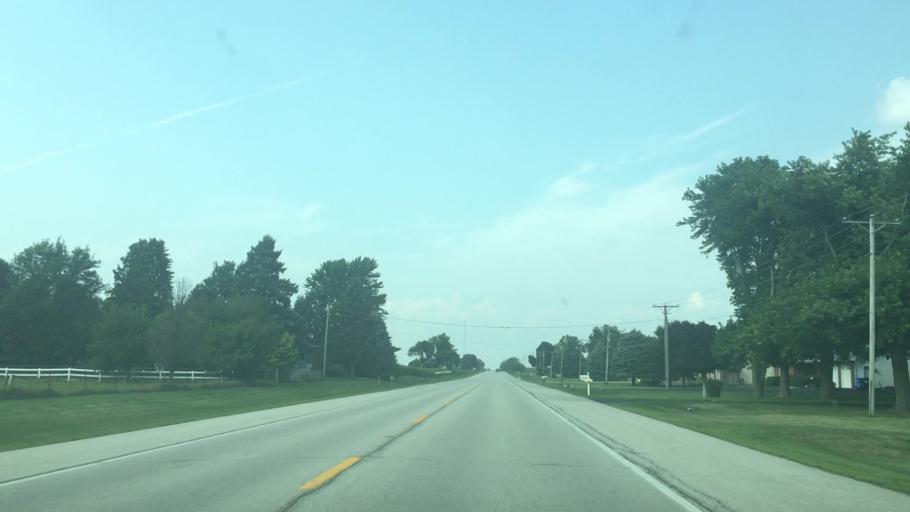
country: US
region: Illinois
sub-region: DeKalb County
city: DeKalb
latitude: 41.8530
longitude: -88.7539
